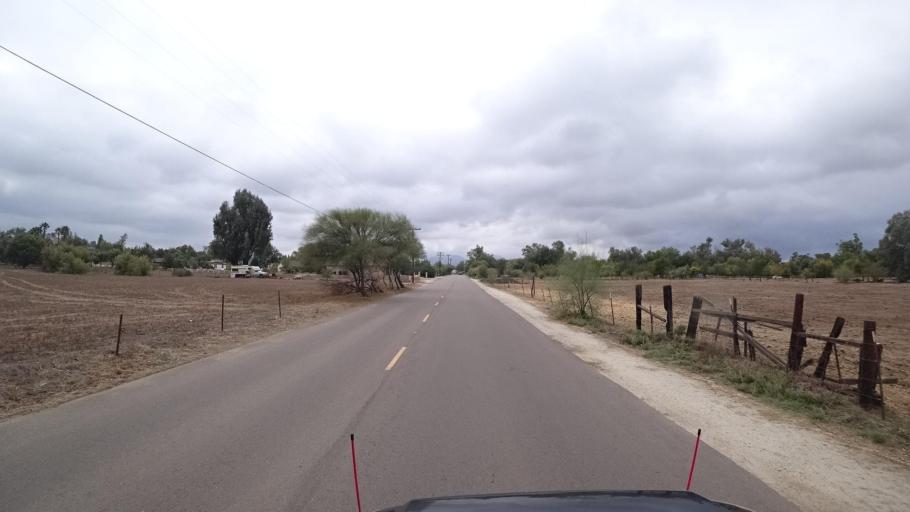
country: US
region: California
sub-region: San Diego County
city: Ramona
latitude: 33.0311
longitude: -116.8772
